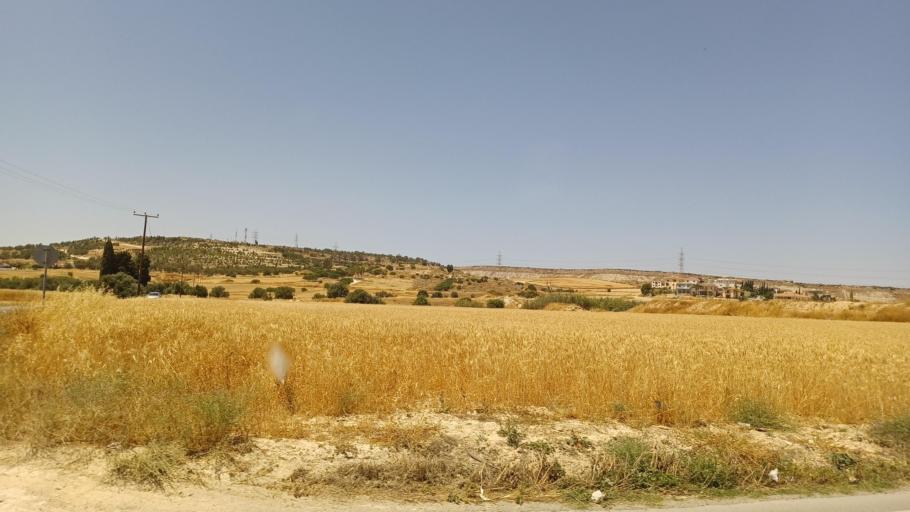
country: CY
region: Larnaka
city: Pyla
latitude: 34.9992
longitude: 33.6885
